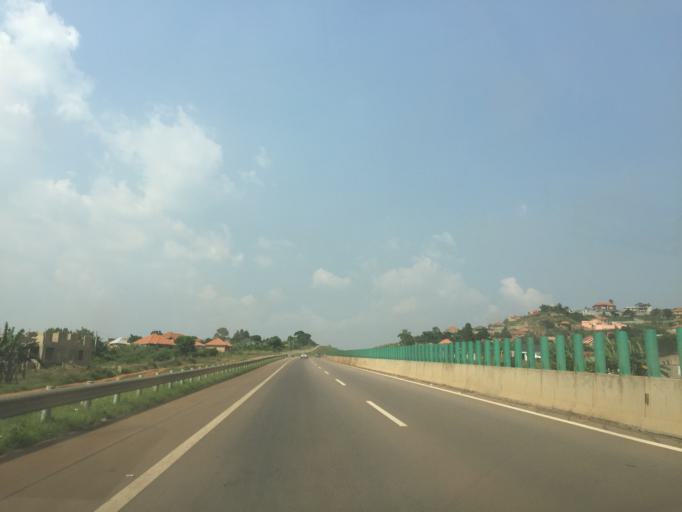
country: UG
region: Central Region
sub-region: Wakiso District
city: Kajansi
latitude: 0.1689
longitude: 32.5144
